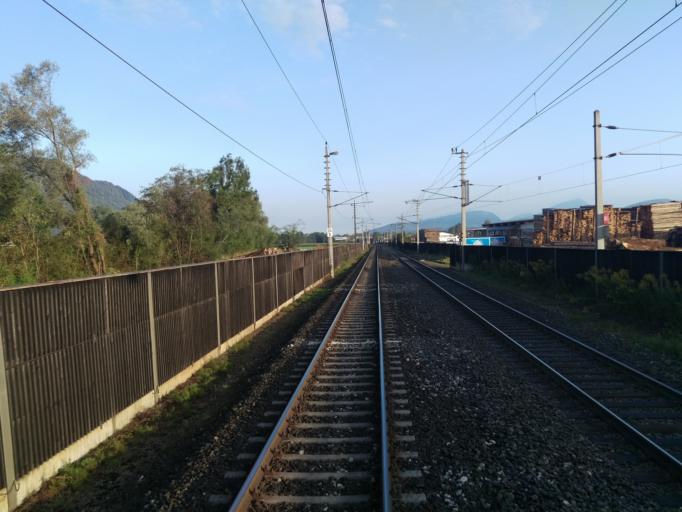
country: AT
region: Salzburg
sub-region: Politischer Bezirk Hallein
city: Kuchl
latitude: 47.6310
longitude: 13.1394
